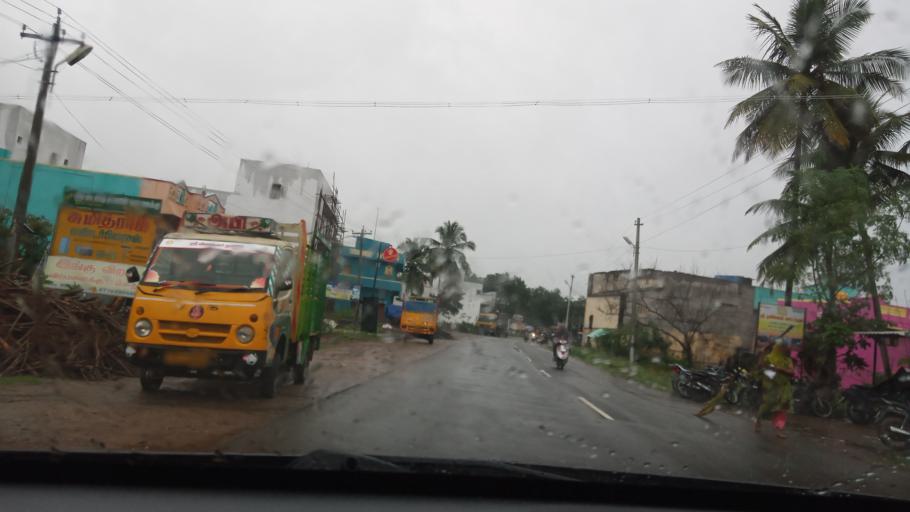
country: IN
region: Tamil Nadu
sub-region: Tiruvannamalai
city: Cheyyar
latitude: 12.6752
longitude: 79.5362
